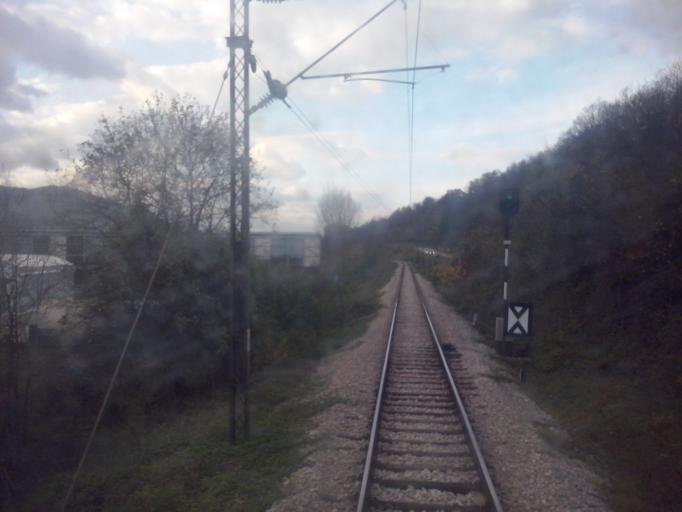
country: RS
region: Central Serbia
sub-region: Zlatiborski Okrug
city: Kosjeric
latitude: 43.9880
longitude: 19.9256
